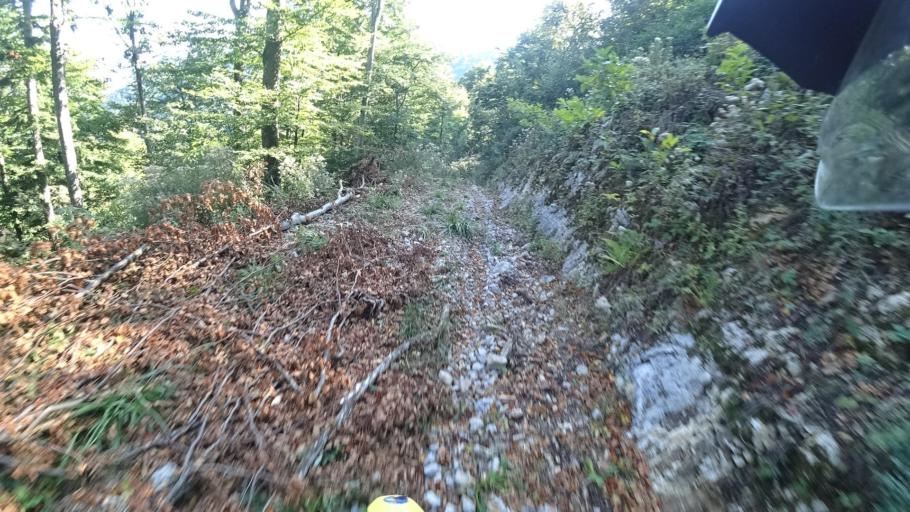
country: HR
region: Primorsko-Goranska
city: Vrbovsko
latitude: 45.2826
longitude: 15.1232
